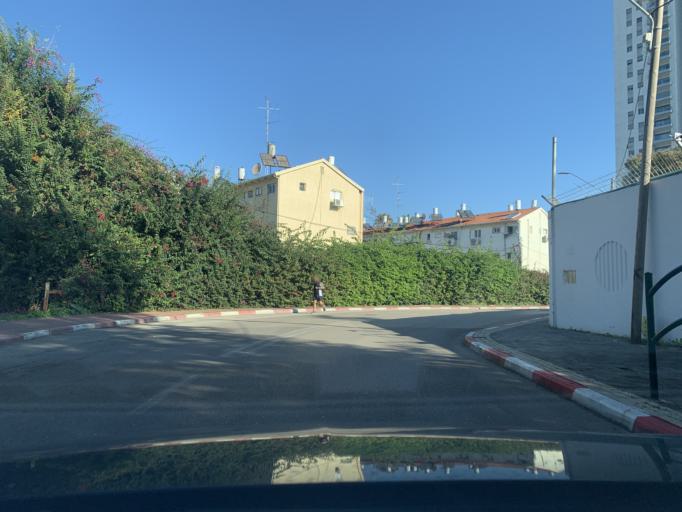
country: IL
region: Tel Aviv
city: Azor
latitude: 32.0470
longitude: 34.8156
